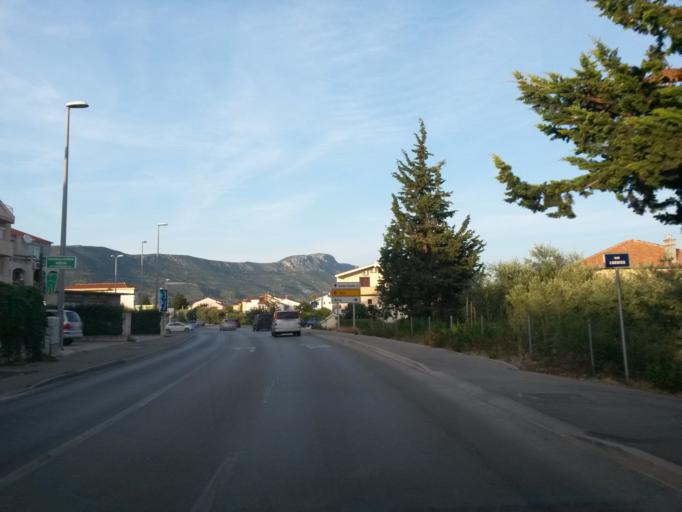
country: HR
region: Splitsko-Dalmatinska
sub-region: Grad Trogir
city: Trogir
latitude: 43.5473
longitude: 16.3233
